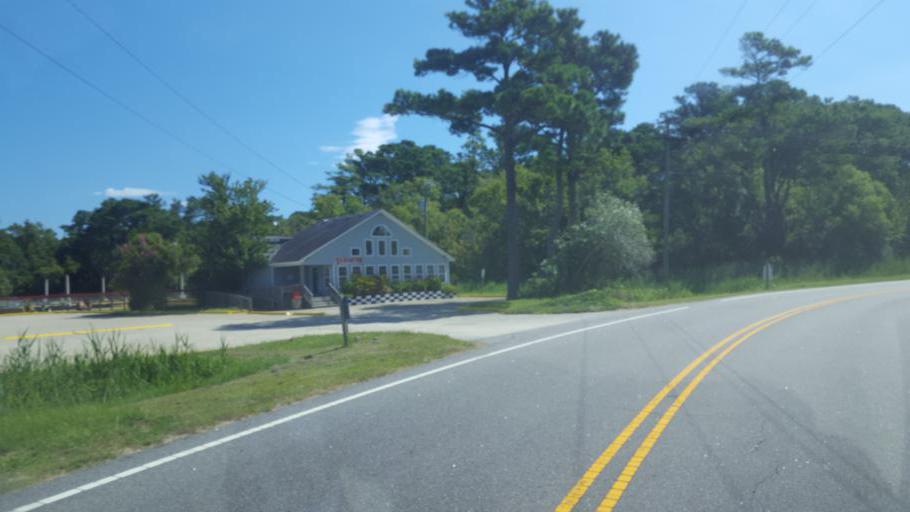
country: US
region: North Carolina
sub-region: Dare County
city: Kill Devil Hills
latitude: 36.0145
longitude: -75.6794
